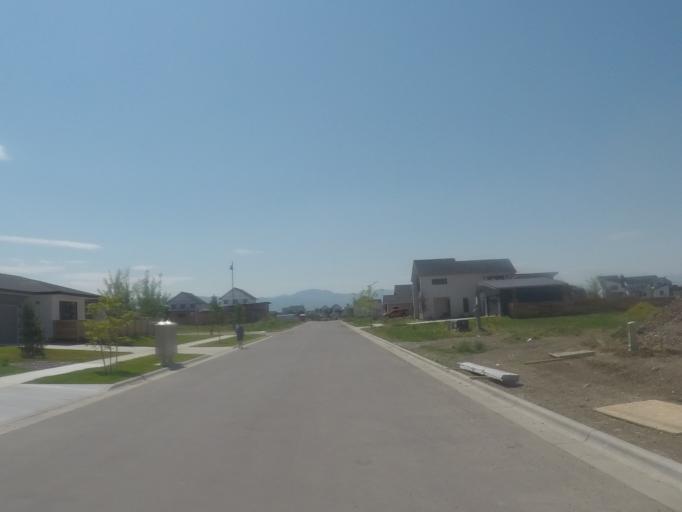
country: US
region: Montana
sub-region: Gallatin County
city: Bozeman
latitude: 45.6912
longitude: -111.0961
